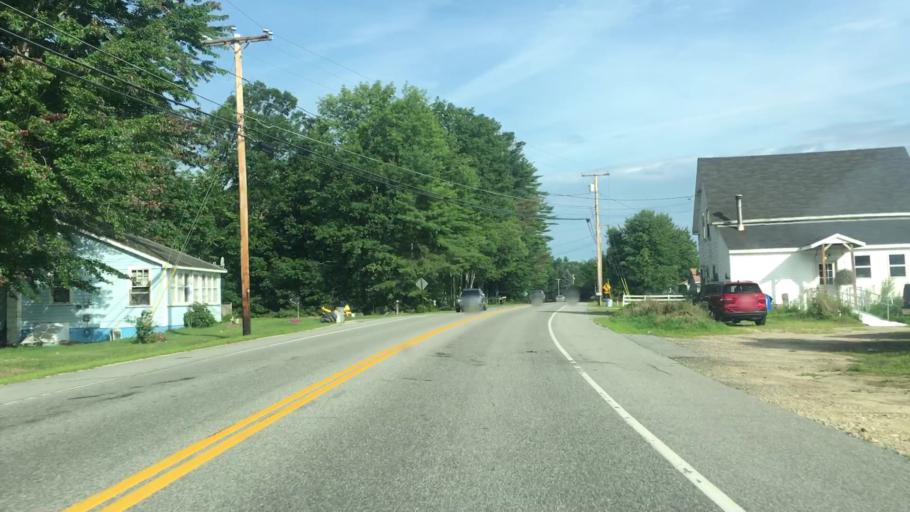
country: US
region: Maine
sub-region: York County
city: Limington
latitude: 43.7355
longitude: -70.6656
